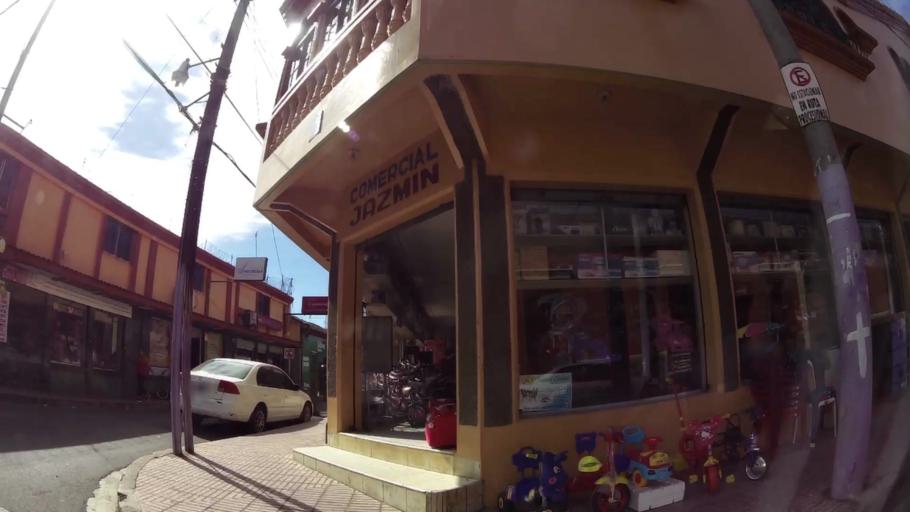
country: SV
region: Santa Ana
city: Chalchuapa
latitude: 13.9852
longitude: -89.6790
